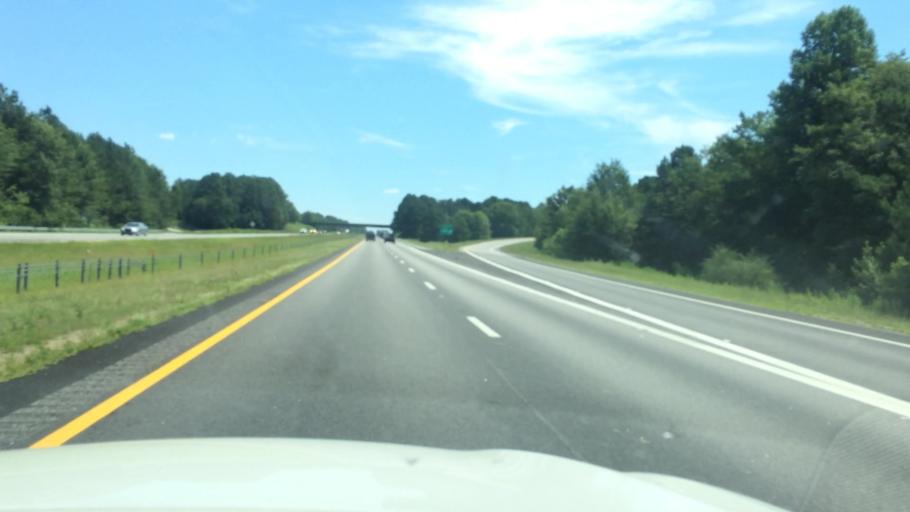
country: US
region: South Carolina
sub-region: Lexington County
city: Leesville
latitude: 33.8125
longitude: -81.4560
